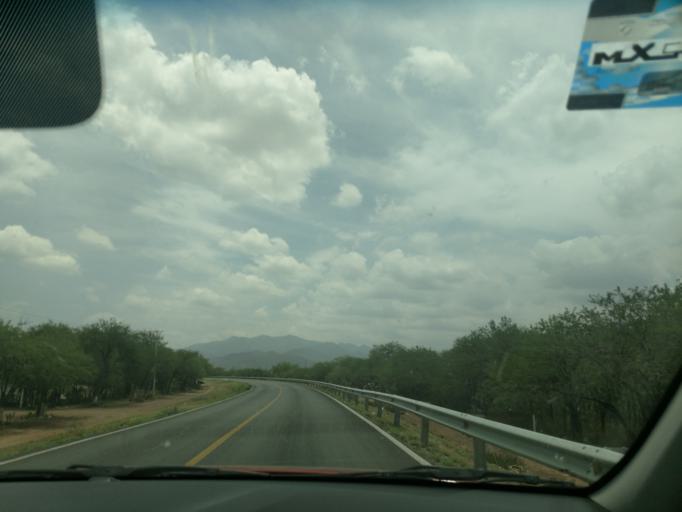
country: MX
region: San Luis Potosi
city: Zaragoza
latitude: 22.0208
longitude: -100.4020
